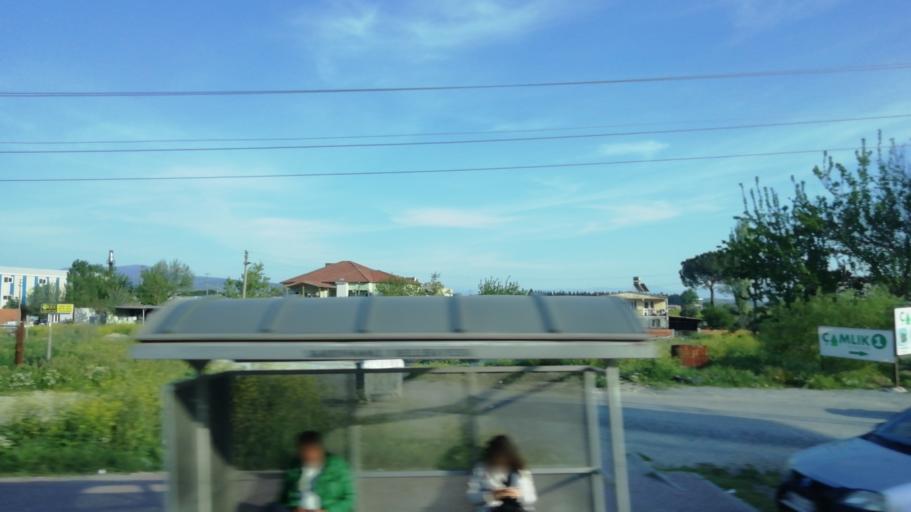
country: TR
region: Manisa
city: Saruhanli
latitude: 38.7296
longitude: 27.5801
